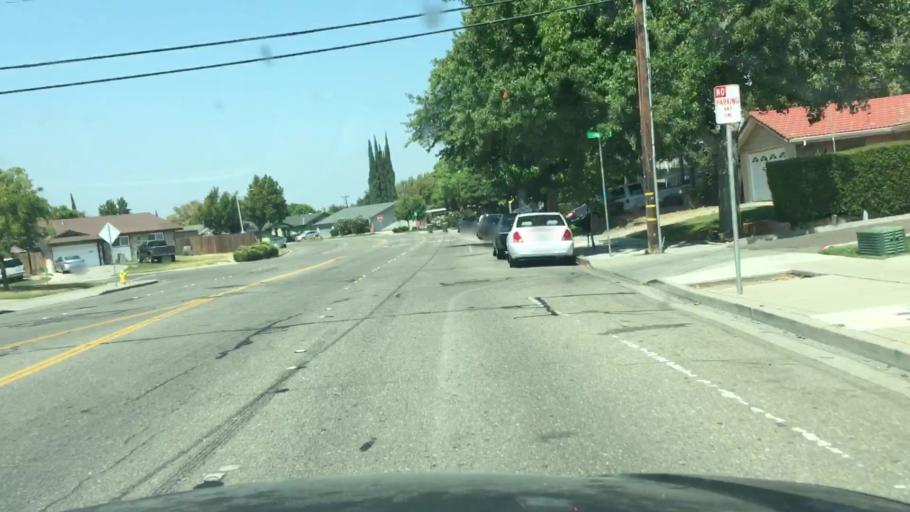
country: US
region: California
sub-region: San Joaquin County
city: Tracy
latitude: 37.7404
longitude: -121.4417
